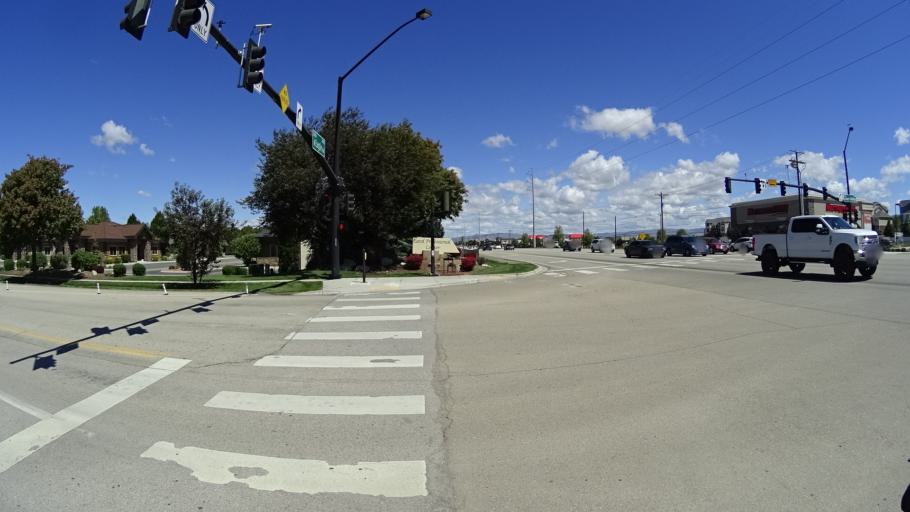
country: US
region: Idaho
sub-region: Ada County
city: Meridian
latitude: 43.6264
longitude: -116.3548
